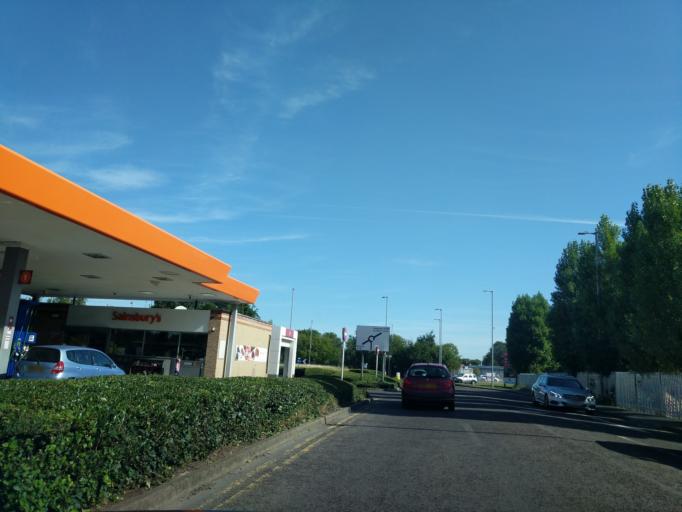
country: GB
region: England
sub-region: Lincolnshire
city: Spalding
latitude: 52.7897
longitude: -0.1556
